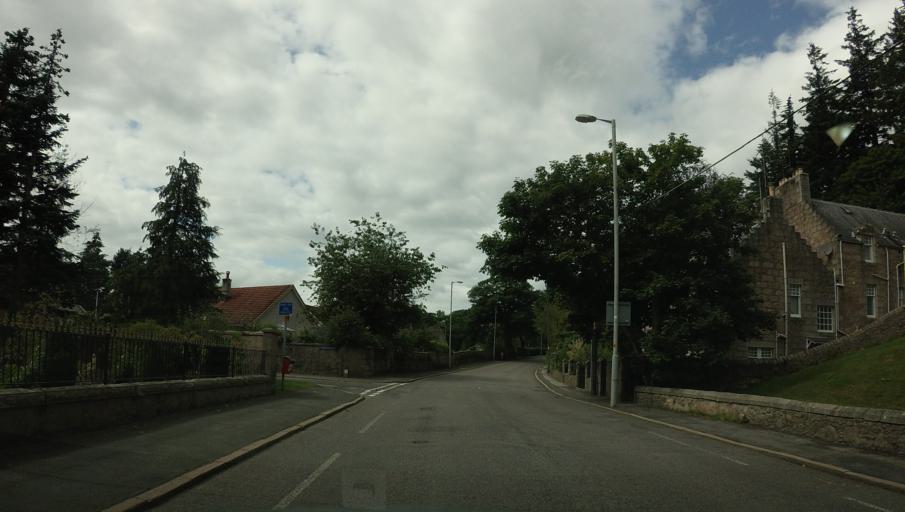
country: GB
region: Scotland
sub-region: Aberdeenshire
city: Ballater
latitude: 57.0507
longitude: -3.0505
